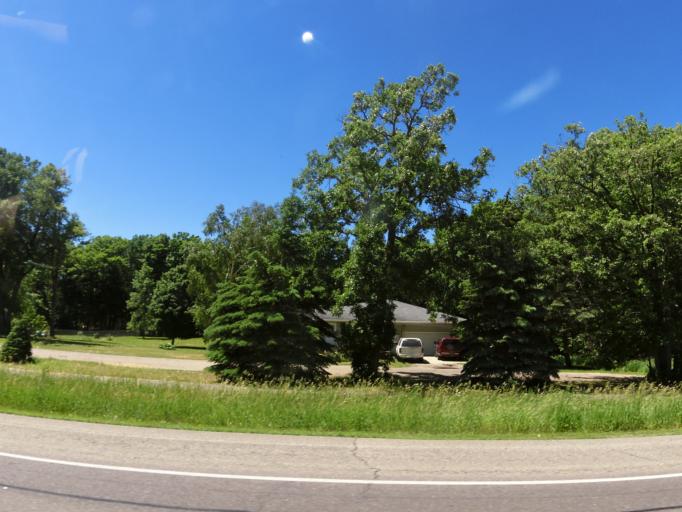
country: US
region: Minnesota
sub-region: Becker County
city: Detroit Lakes
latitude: 46.7981
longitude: -95.8075
